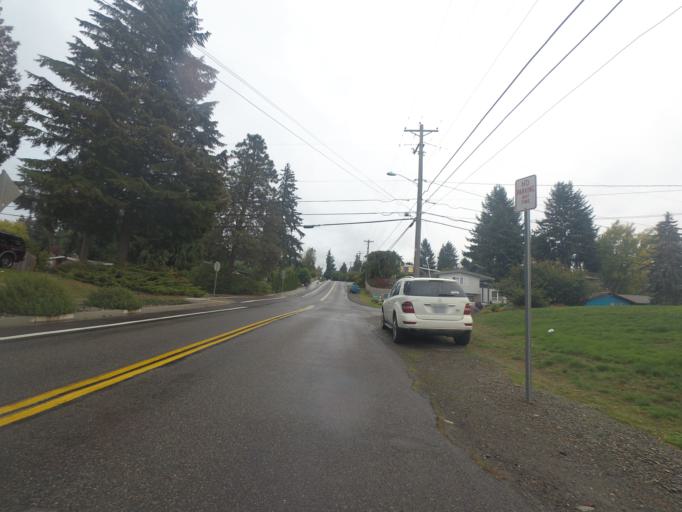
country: US
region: Washington
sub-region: Pierce County
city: University Place
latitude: 47.2199
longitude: -122.5512
